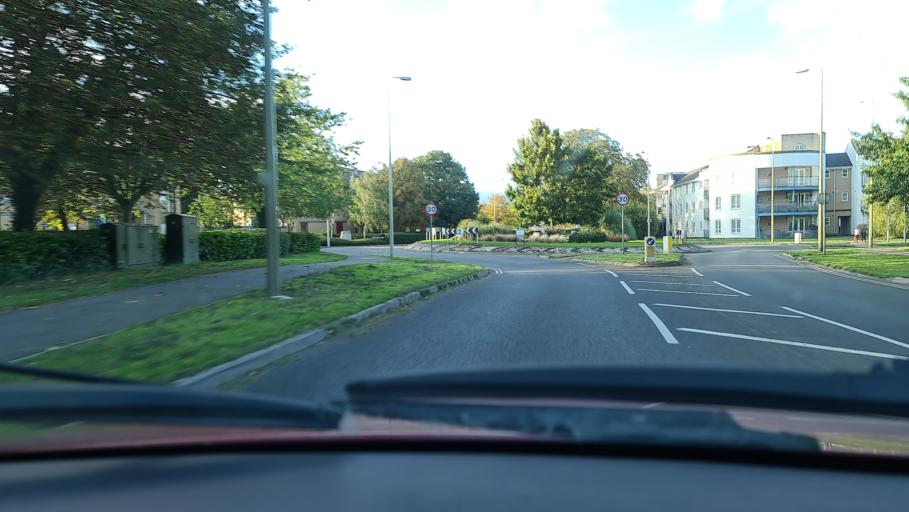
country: GB
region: England
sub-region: Oxfordshire
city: Bicester
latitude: 51.8909
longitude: -1.1476
